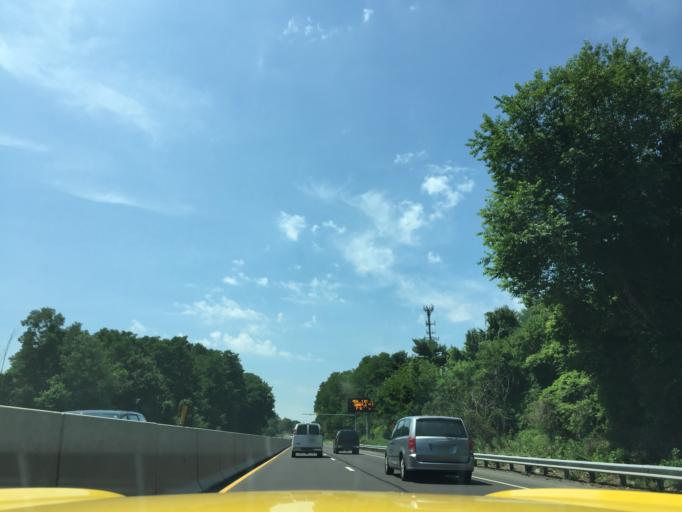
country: US
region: Pennsylvania
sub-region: Bucks County
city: Woodbourne
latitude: 40.1844
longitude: -74.9007
